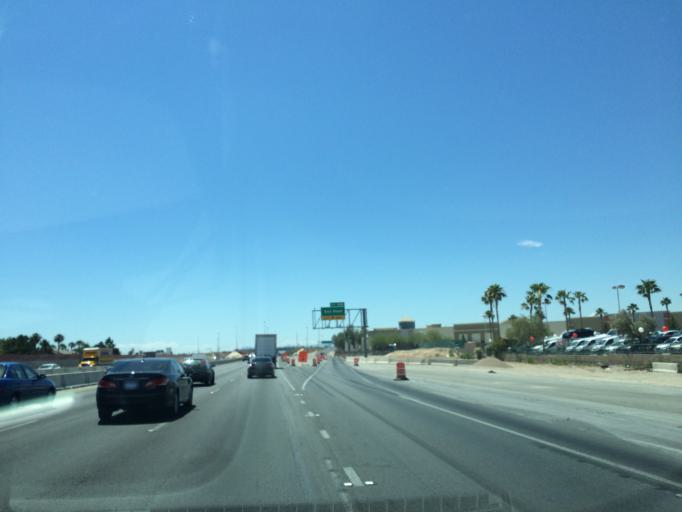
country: US
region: Nevada
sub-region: Clark County
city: Las Vegas
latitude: 36.2686
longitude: -115.2589
